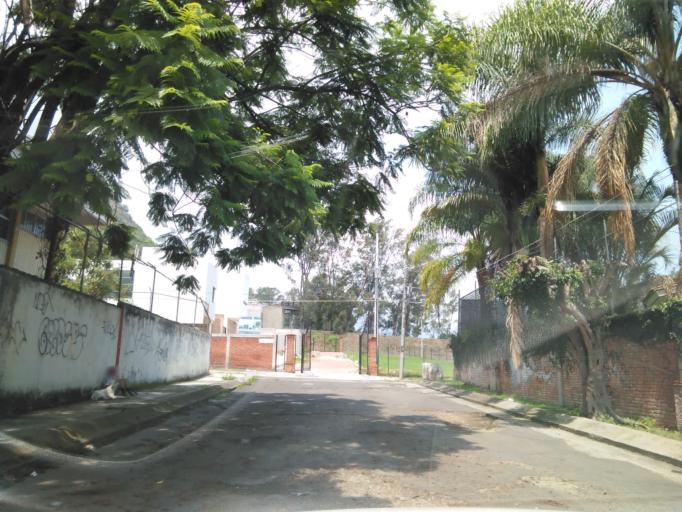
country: MX
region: Nayarit
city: Tepic
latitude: 21.5148
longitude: -104.9231
